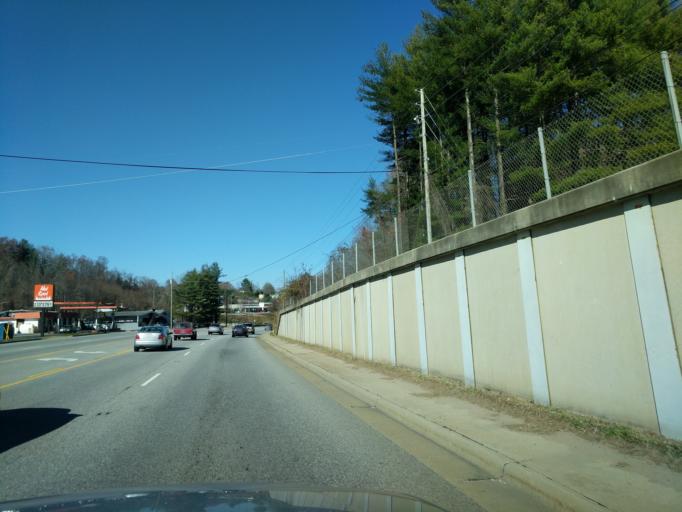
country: US
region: North Carolina
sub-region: Buncombe County
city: Biltmore Forest
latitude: 35.5444
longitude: -82.5216
